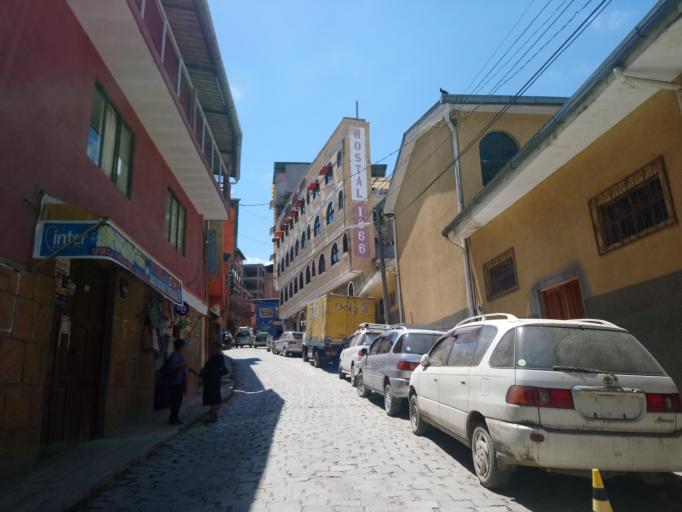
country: BO
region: La Paz
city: Coroico
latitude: -16.1886
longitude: -67.7272
